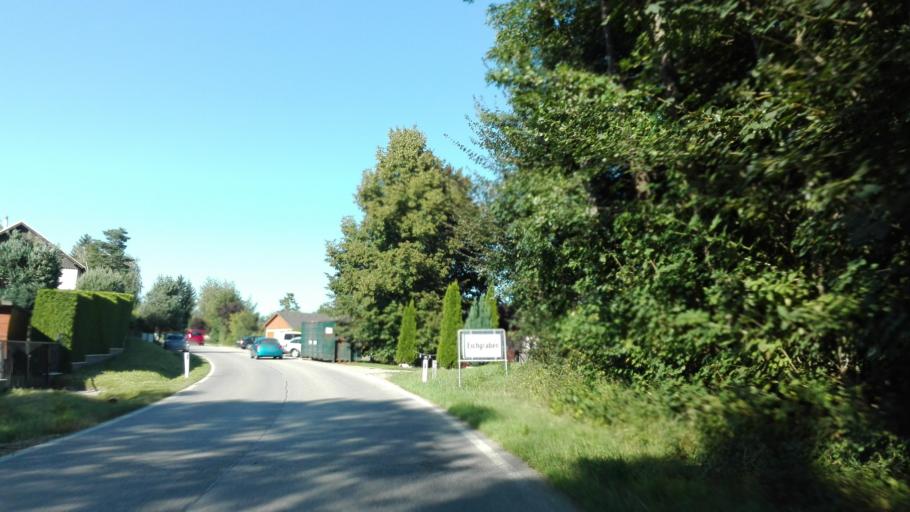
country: AT
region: Lower Austria
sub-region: Politischer Bezirk Sankt Polten
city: Eichgraben
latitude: 48.1573
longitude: 15.9673
